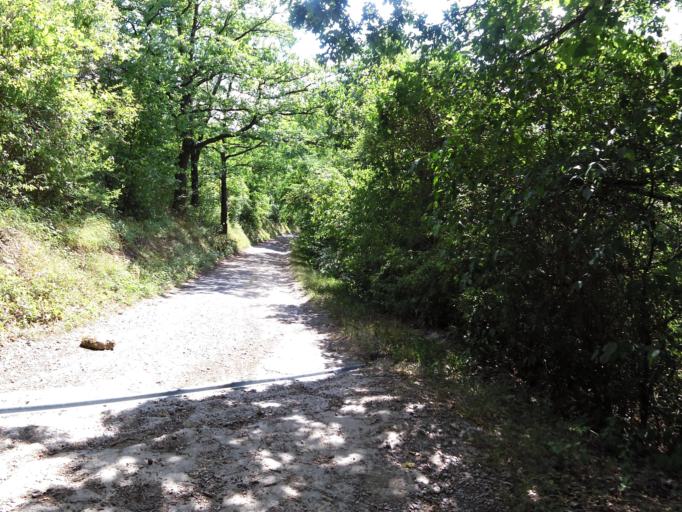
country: DE
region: Bavaria
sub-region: Regierungsbezirk Unterfranken
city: Gerbrunn
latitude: 49.7809
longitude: 9.9968
